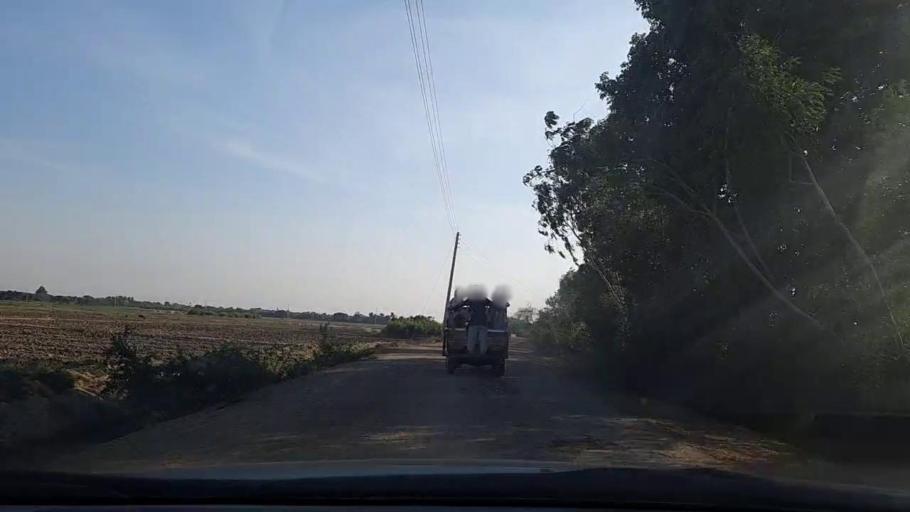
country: PK
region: Sindh
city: Mirpur Sakro
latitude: 24.5308
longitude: 67.6330
